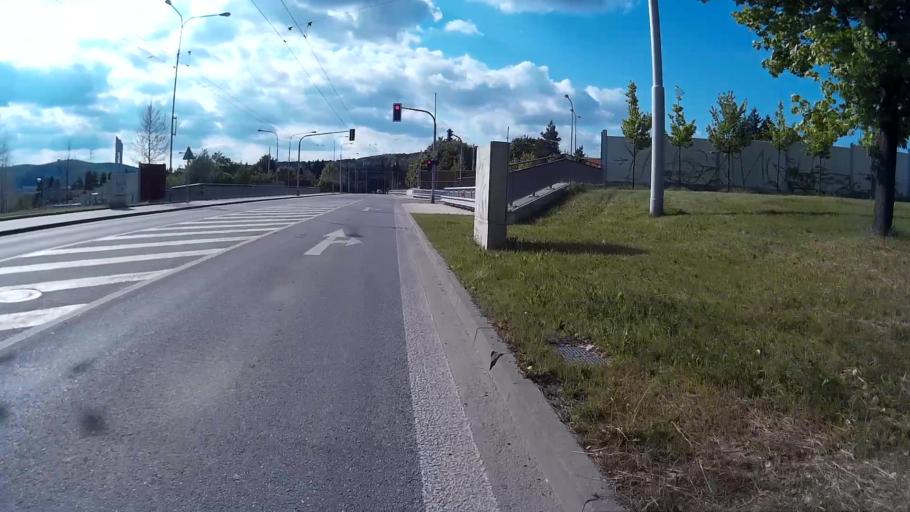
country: CZ
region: South Moravian
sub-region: Mesto Brno
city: Brno
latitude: 49.2159
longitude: 16.5815
